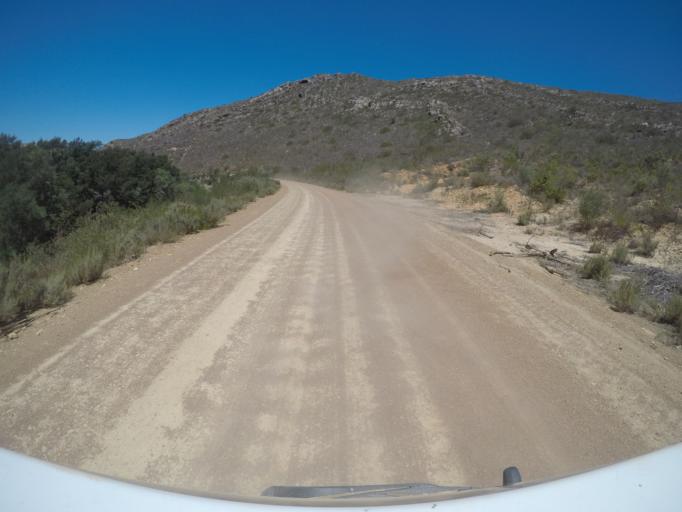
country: ZA
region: Western Cape
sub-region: Overberg District Municipality
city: Caledon
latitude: -34.1197
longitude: 19.2354
